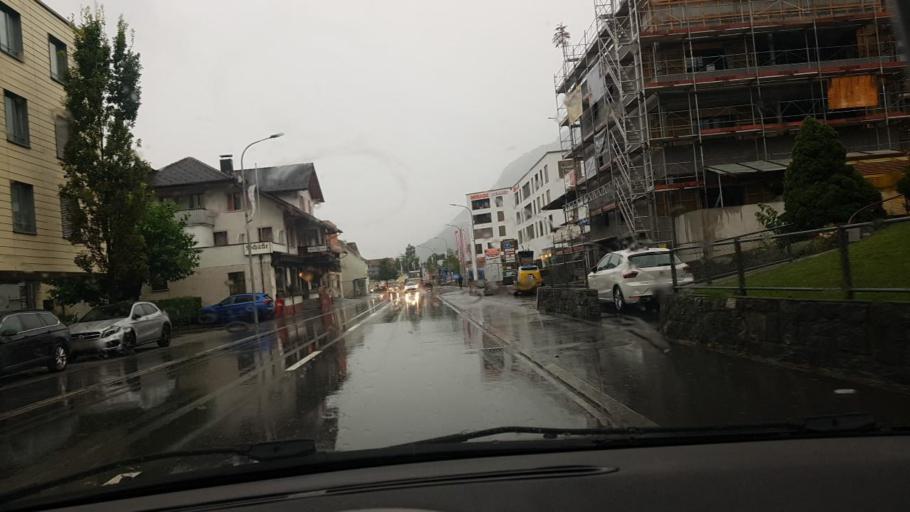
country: LI
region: Triesen
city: Triesen
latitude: 47.1078
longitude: 9.5251
